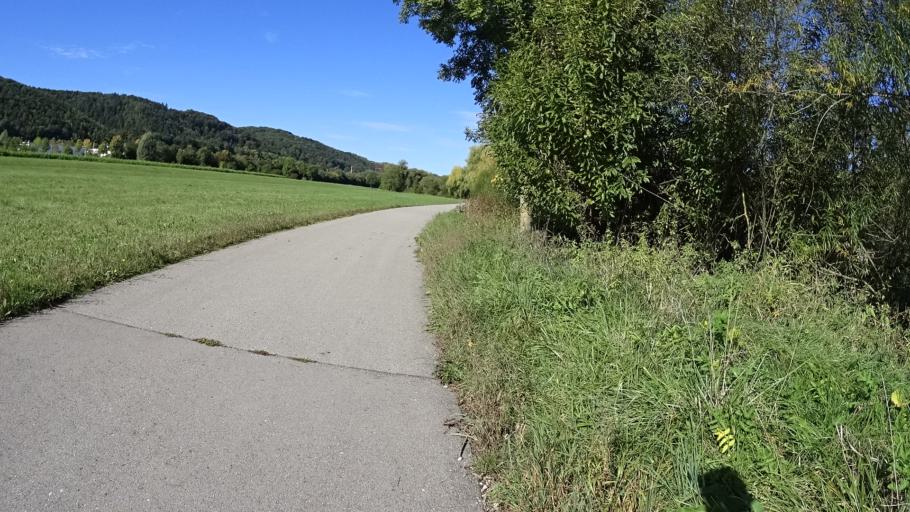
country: DE
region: Bavaria
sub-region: Upper Bavaria
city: Eichstaett
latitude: 48.8796
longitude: 11.2151
